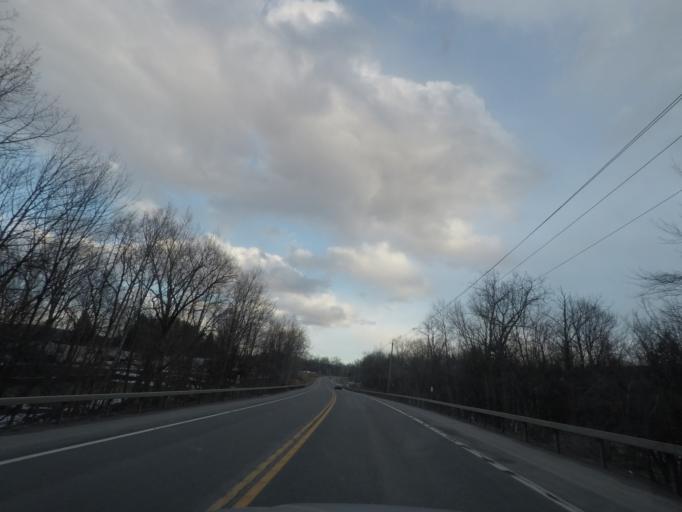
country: US
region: New York
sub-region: Herkimer County
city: Frankfort
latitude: 43.0826
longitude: -75.1207
